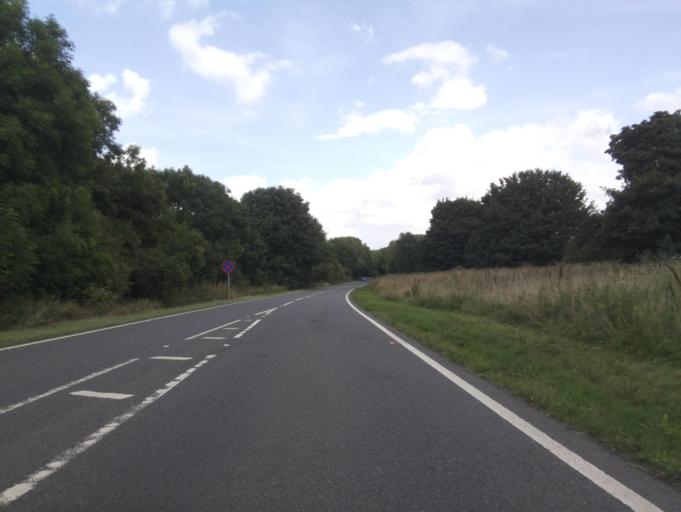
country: GB
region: England
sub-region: Darlington
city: High Coniscliffe
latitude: 54.4592
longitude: -1.6665
